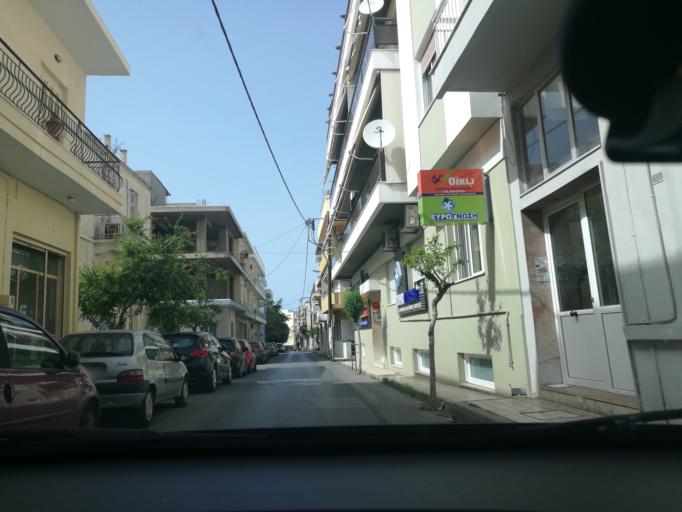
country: GR
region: Crete
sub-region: Nomos Irakleiou
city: Irakleion
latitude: 35.3270
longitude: 25.1306
